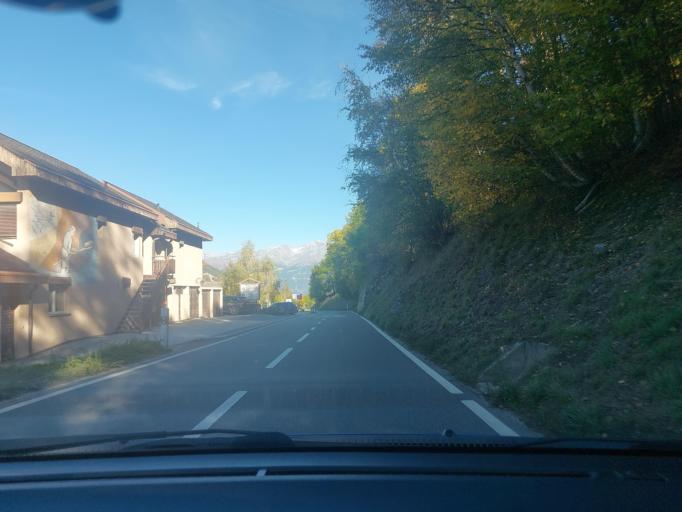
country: CH
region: Valais
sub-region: Sierre District
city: Chippis
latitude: 46.2200
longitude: 7.5830
